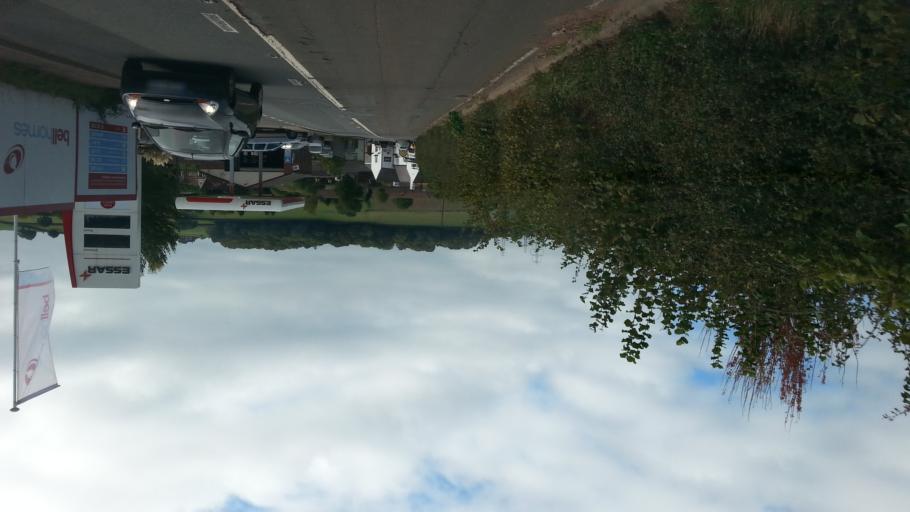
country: GB
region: England
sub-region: Herefordshire
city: Lea
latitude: 51.8935
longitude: -2.4949
